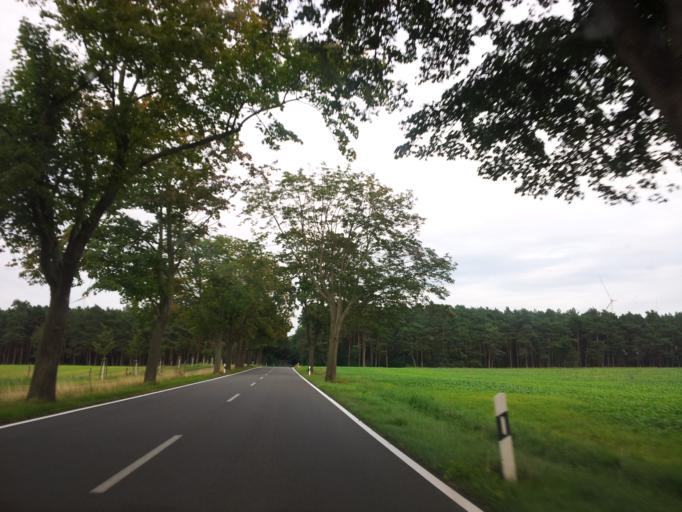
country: DE
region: Brandenburg
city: Linthe
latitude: 52.0915
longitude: 12.7613
